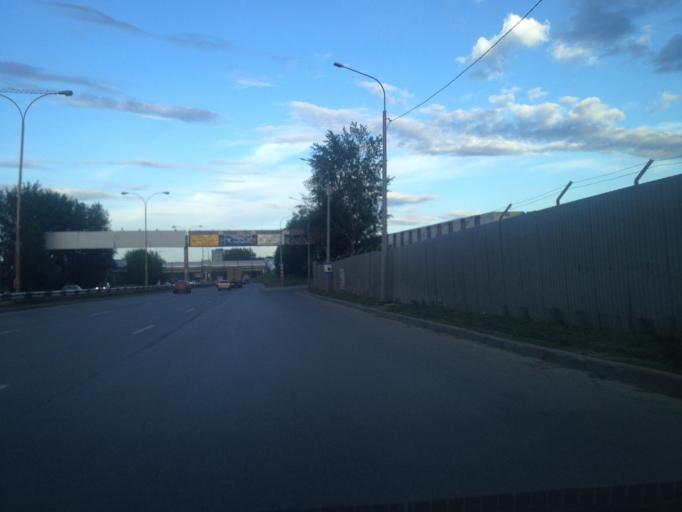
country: RU
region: Sverdlovsk
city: Yekaterinburg
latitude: 56.7899
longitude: 60.6130
